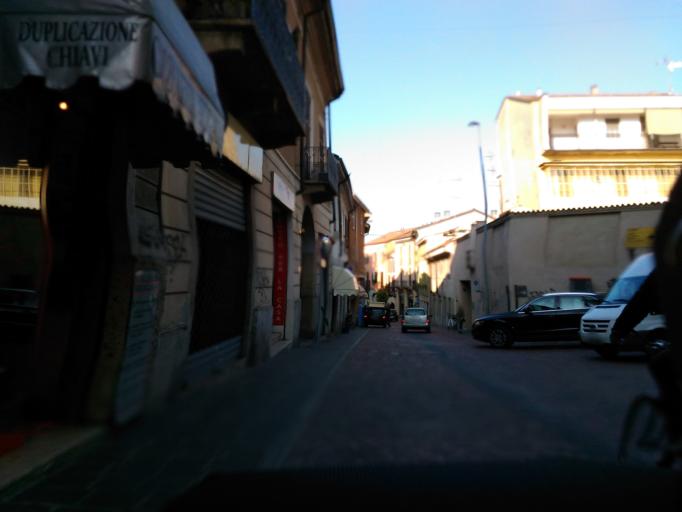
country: IT
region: Lombardy
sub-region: Provincia di Lodi
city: Lodi
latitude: 45.3160
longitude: 9.5059
